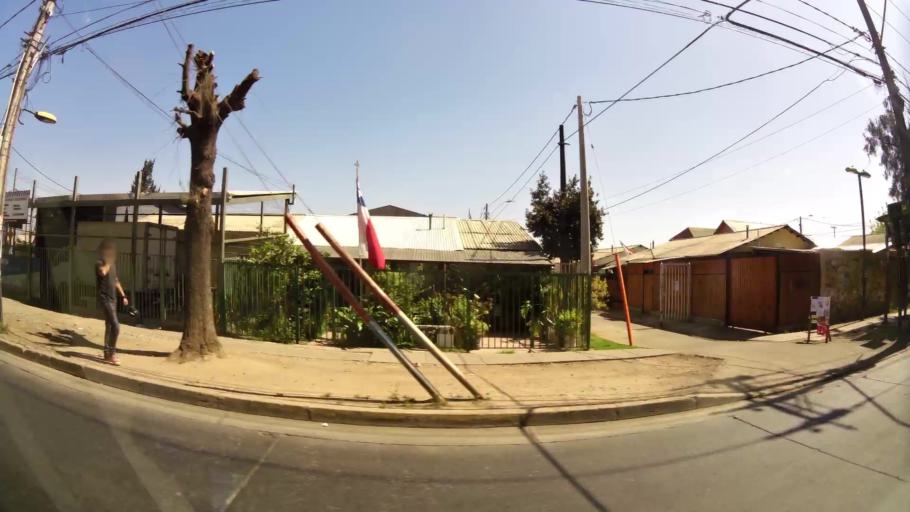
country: CL
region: Santiago Metropolitan
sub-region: Provincia de Santiago
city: Lo Prado
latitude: -33.4925
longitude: -70.7434
